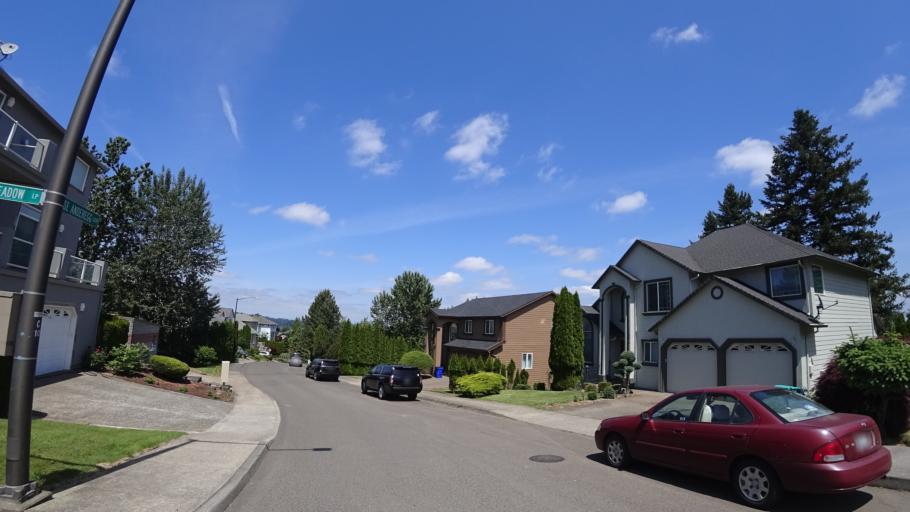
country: US
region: Oregon
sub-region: Clackamas County
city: Happy Valley
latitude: 45.4897
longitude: -122.4935
